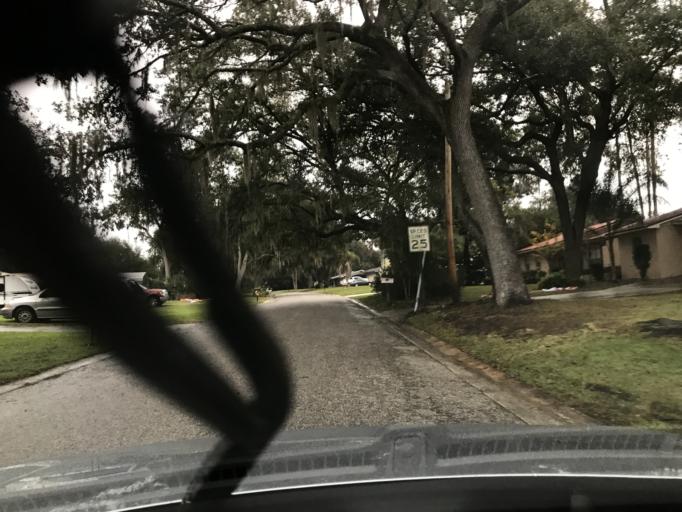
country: US
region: Florida
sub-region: Hillsborough County
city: Plant City
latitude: 28.0382
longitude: -82.1002
